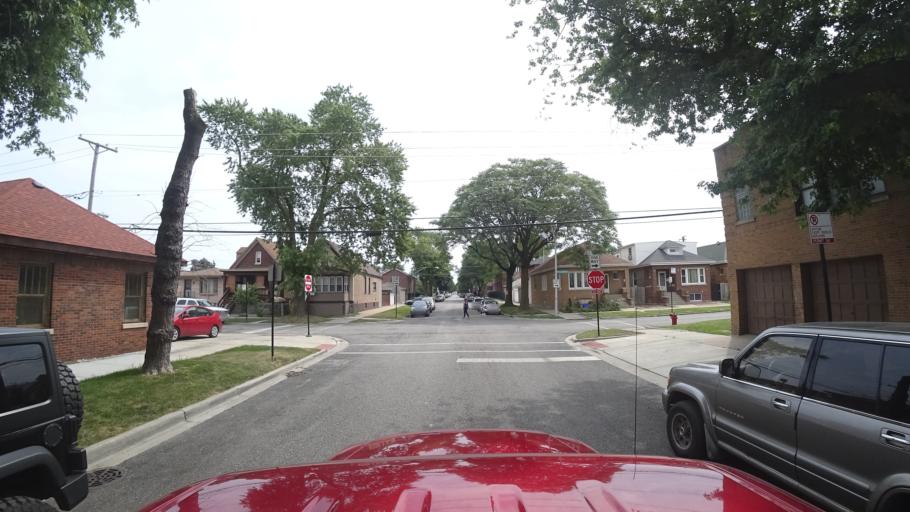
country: US
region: Illinois
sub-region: Cook County
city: Chicago
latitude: 41.8321
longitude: -87.6841
